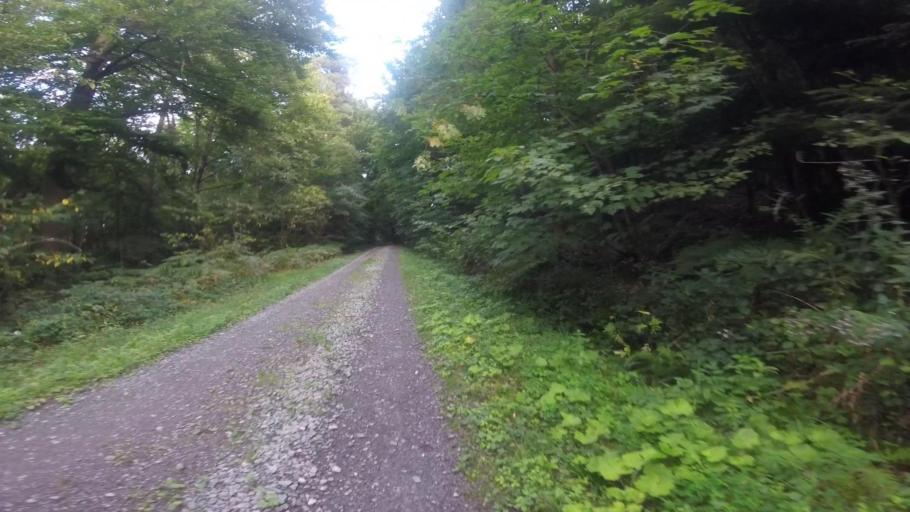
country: DE
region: Baden-Wuerttemberg
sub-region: Regierungsbezirk Stuttgart
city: Oberstenfeld
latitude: 49.0312
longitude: 9.3534
